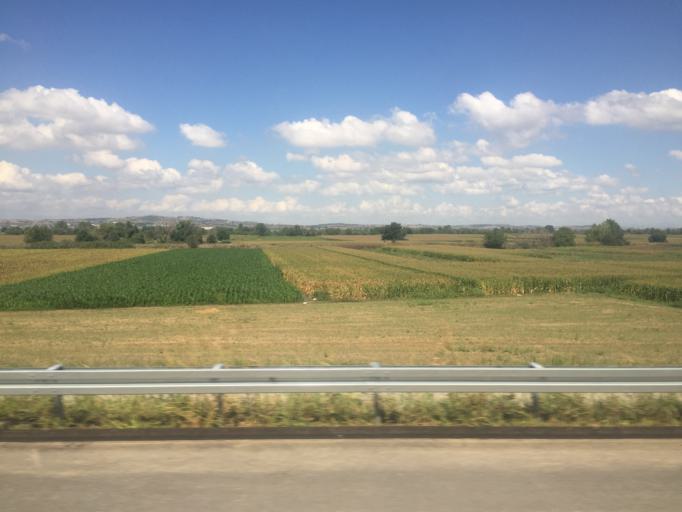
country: TR
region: Balikesir
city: Gobel
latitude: 40.0186
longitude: 28.2030
